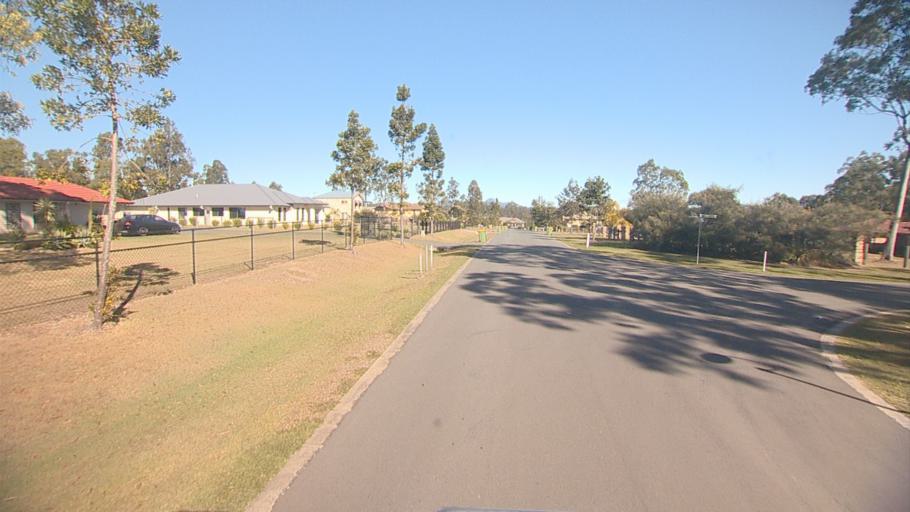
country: AU
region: Queensland
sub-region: Logan
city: North Maclean
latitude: -27.7463
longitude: 152.9494
